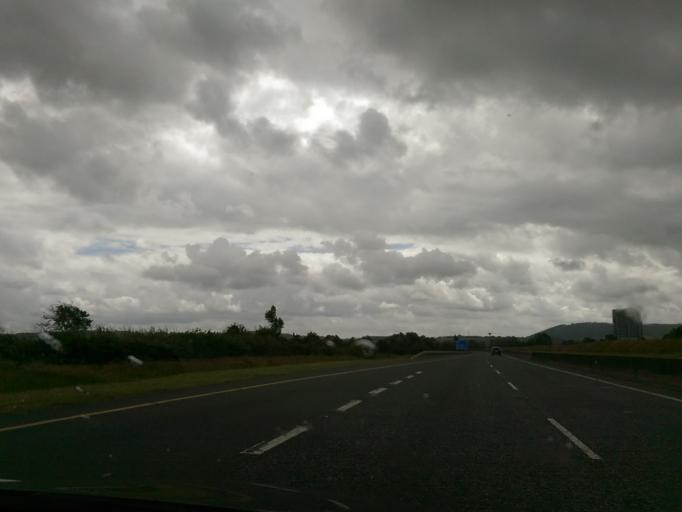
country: IE
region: Munster
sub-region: County Cork
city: Fermoy
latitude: 52.1572
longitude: -8.2657
